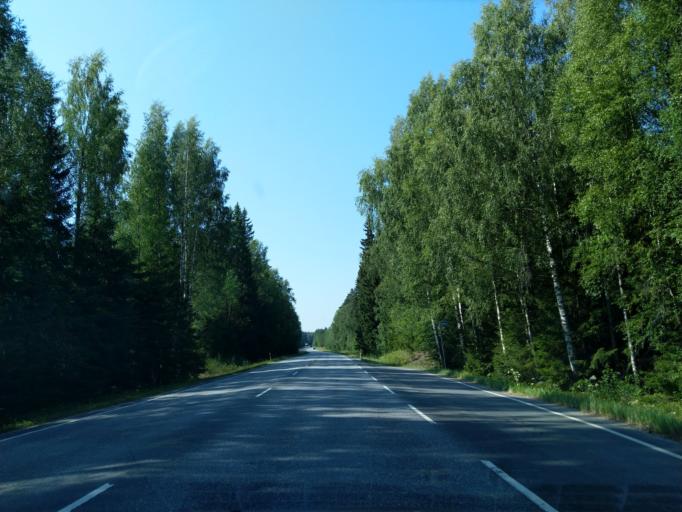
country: FI
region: Satakunta
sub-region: Pori
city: Noormarkku
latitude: 61.6084
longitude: 21.8843
